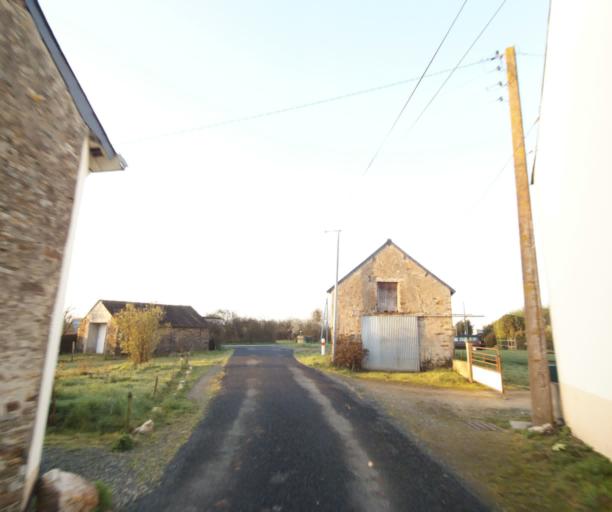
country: FR
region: Pays de la Loire
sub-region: Departement de la Loire-Atlantique
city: Bouvron
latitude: 47.4342
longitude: -1.8939
